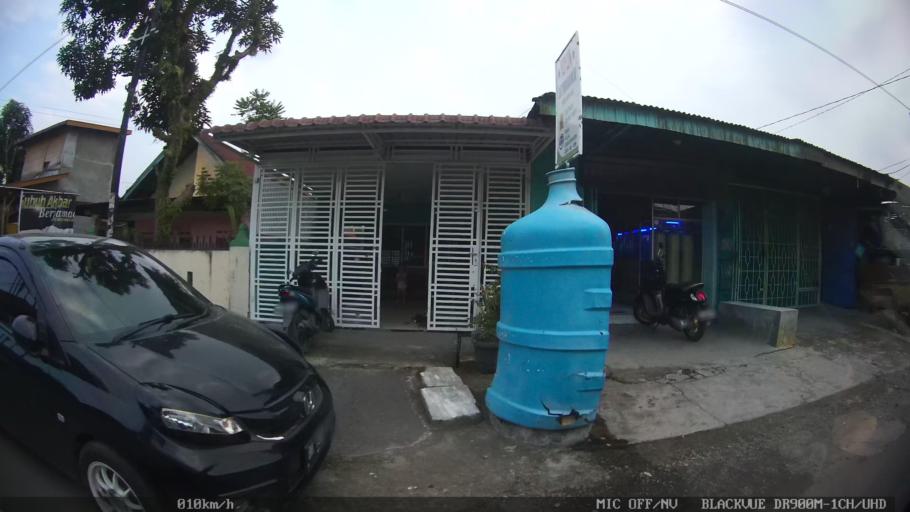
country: ID
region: North Sumatra
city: Medan
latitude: 3.6099
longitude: 98.6857
